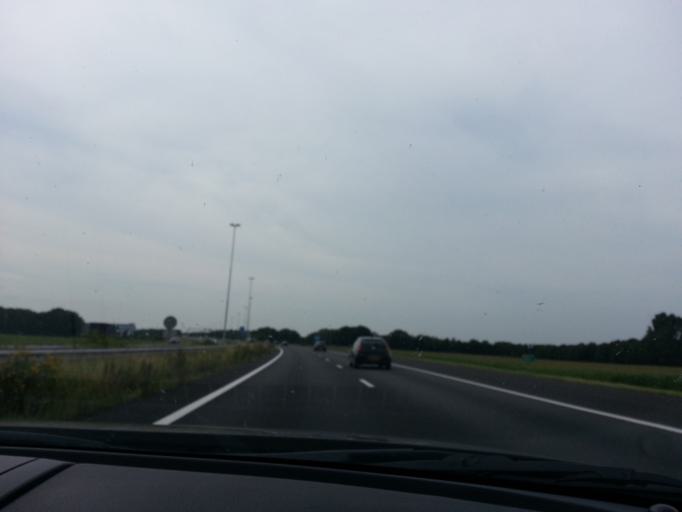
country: NL
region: North Brabant
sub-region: Gemeente Dongen
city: Dongen
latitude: 51.5494
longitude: 4.9692
